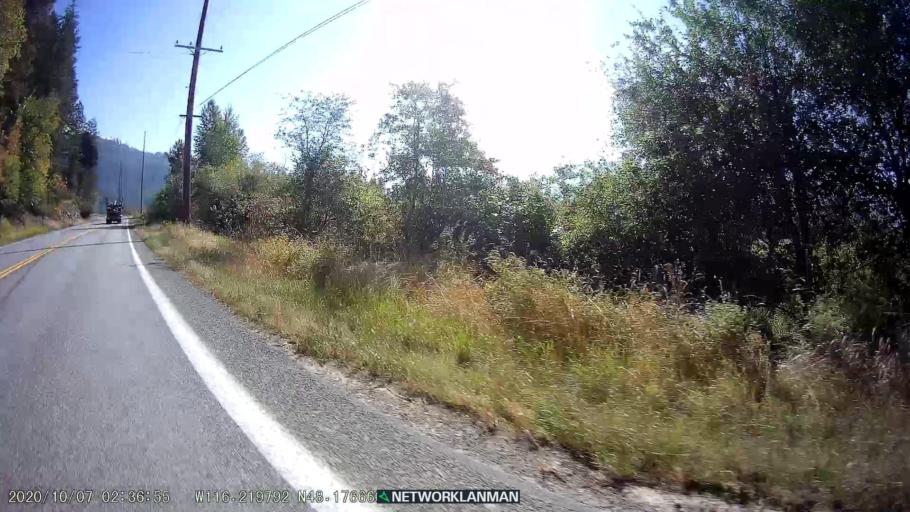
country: US
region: Idaho
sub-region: Bonner County
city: Ponderay
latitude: 48.1766
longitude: -116.2197
